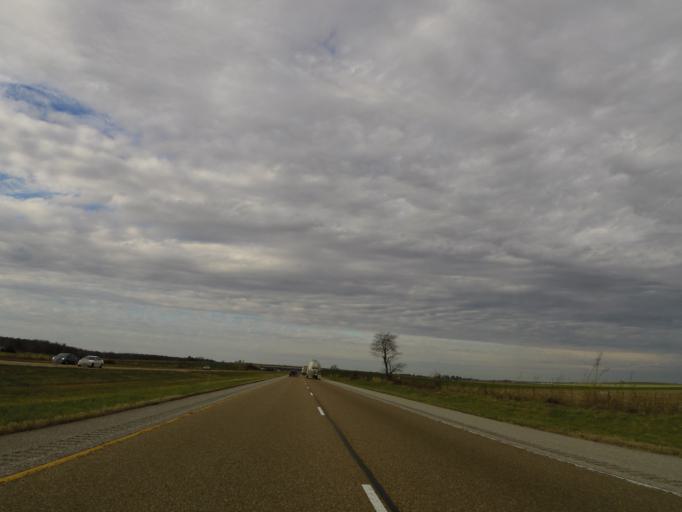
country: US
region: Illinois
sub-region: Washington County
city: Nashville
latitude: 38.3912
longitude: -89.2691
